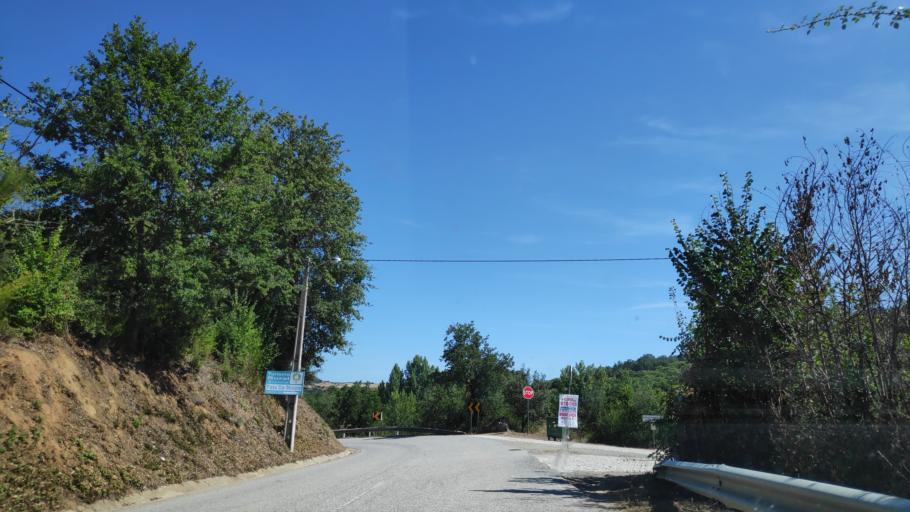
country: PT
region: Braganca
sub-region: Braganca Municipality
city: Braganca
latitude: 41.8469
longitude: -6.7472
